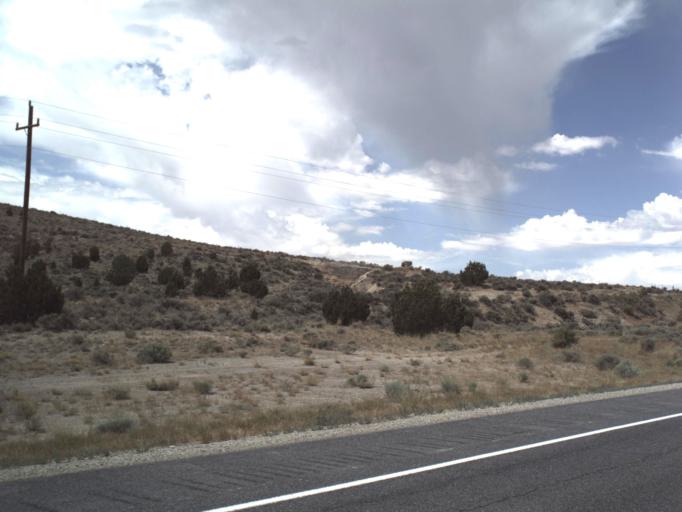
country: US
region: Utah
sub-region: Utah County
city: Eagle Mountain
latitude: 40.0722
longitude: -112.3664
